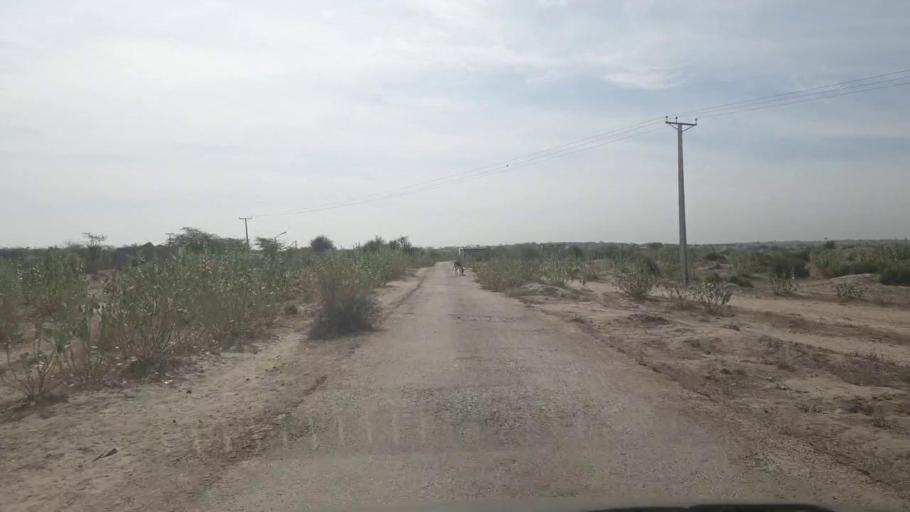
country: PK
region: Sindh
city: Umarkot
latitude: 25.2866
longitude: 69.7416
